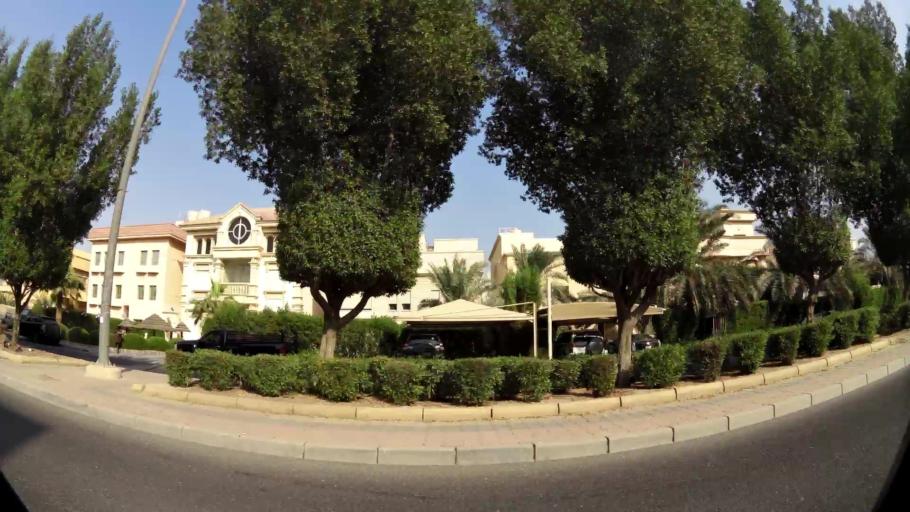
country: KW
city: Bayan
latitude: 29.2806
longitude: 48.0464
